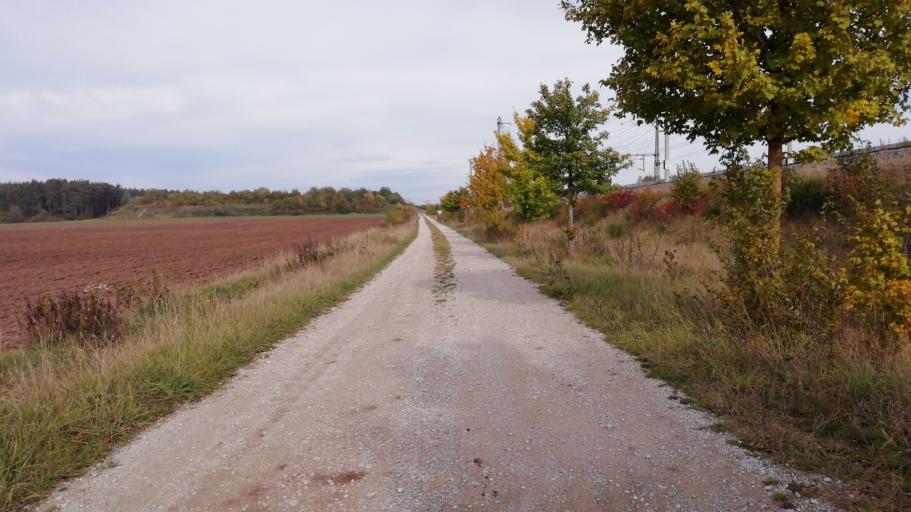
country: DE
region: Bavaria
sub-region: Regierungsbezirk Mittelfranken
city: Allersberg
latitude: 49.2632
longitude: 11.2121
